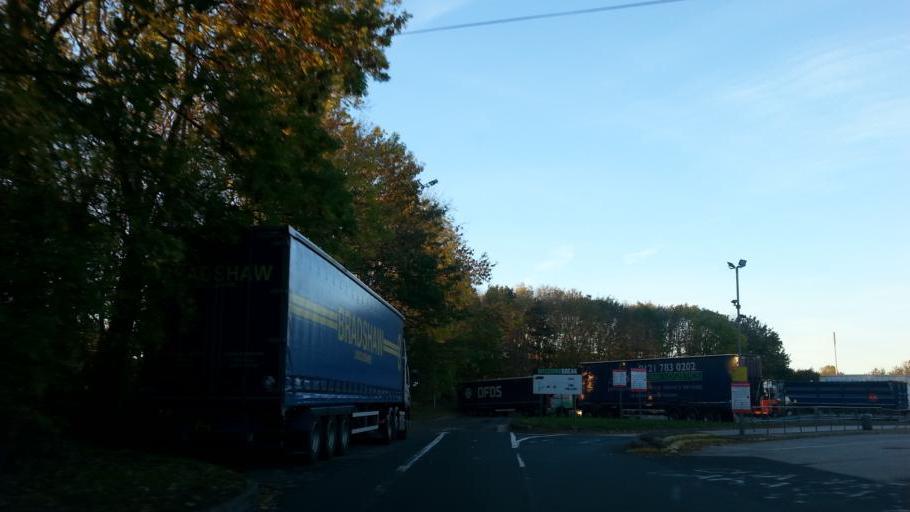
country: GB
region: England
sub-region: Kirklees
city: Cleckheaton
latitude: 53.7127
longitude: -1.7482
